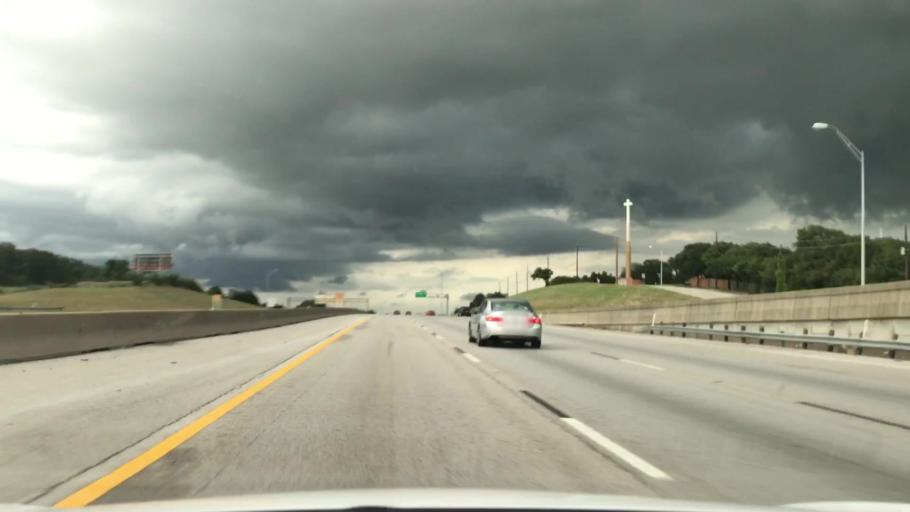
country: US
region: Texas
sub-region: Tarrant County
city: Richland Hills
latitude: 32.7597
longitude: -97.2058
